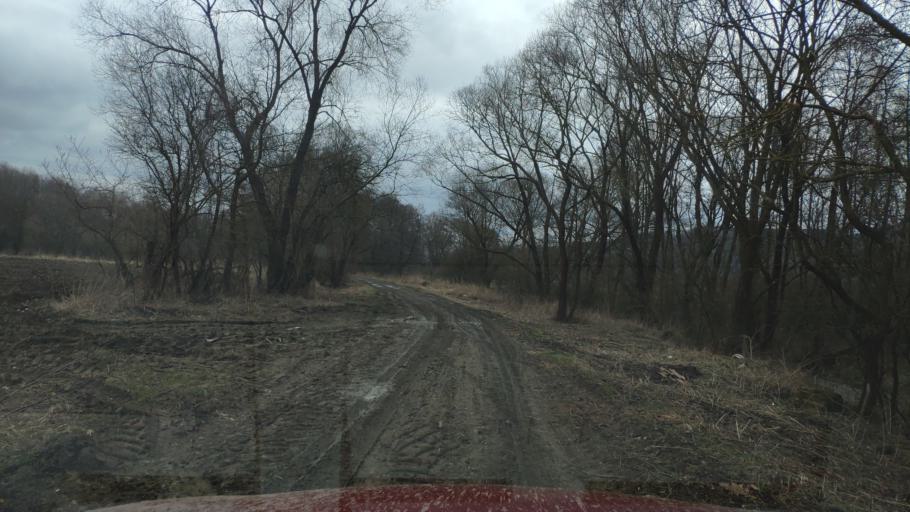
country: SK
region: Presovsky
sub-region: Okres Presov
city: Presov
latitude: 49.0760
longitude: 21.2921
